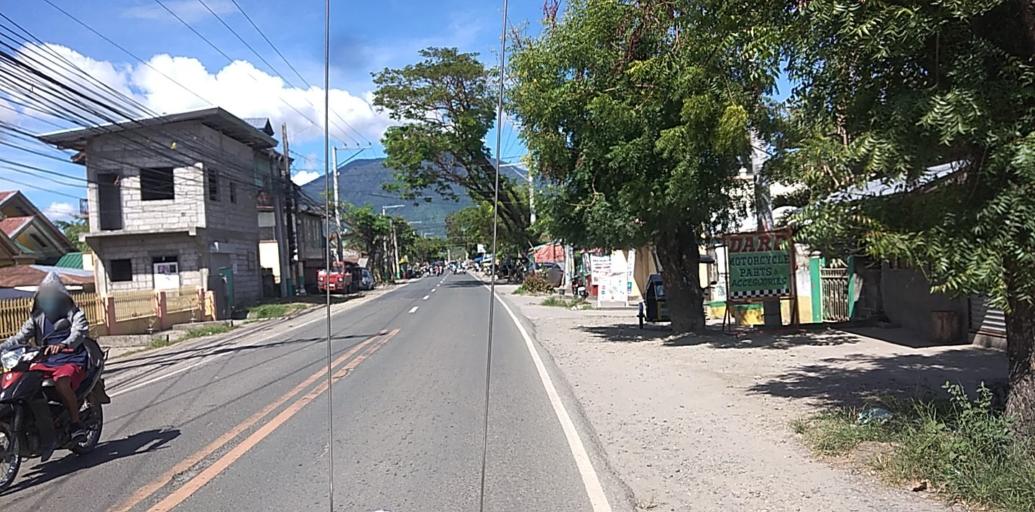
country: PH
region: Central Luzon
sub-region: Province of Pampanga
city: Arayat
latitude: 15.1406
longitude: 120.7727
